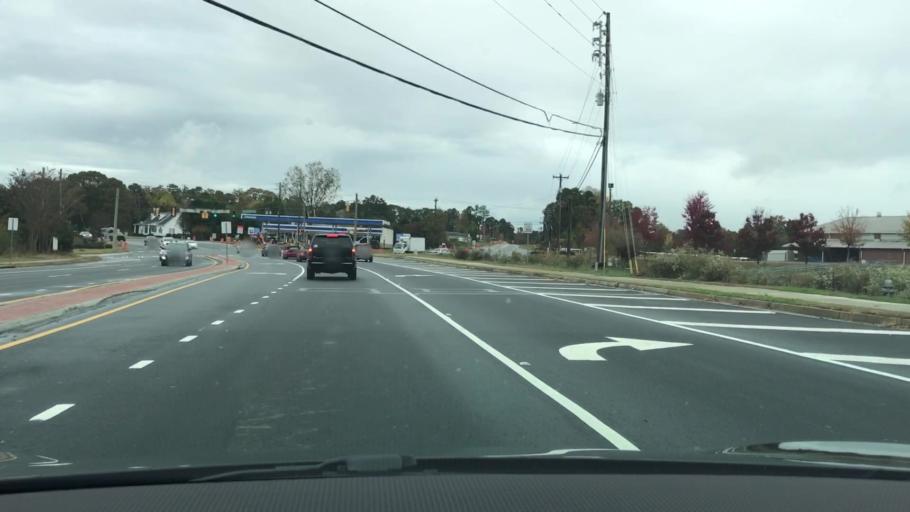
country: US
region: Georgia
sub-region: Forsyth County
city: Cumming
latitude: 34.1139
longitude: -84.1544
